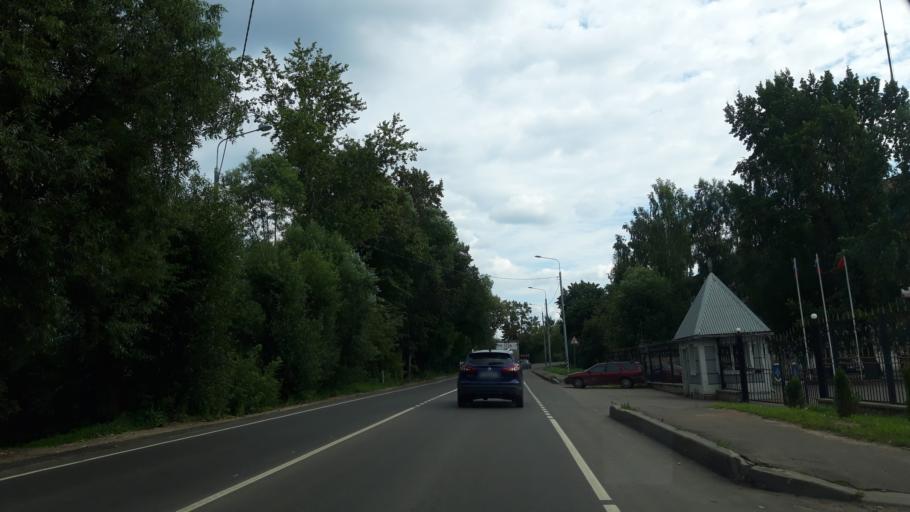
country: RU
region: Moskovskaya
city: Solnechnogorsk
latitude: 56.1974
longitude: 36.9668
